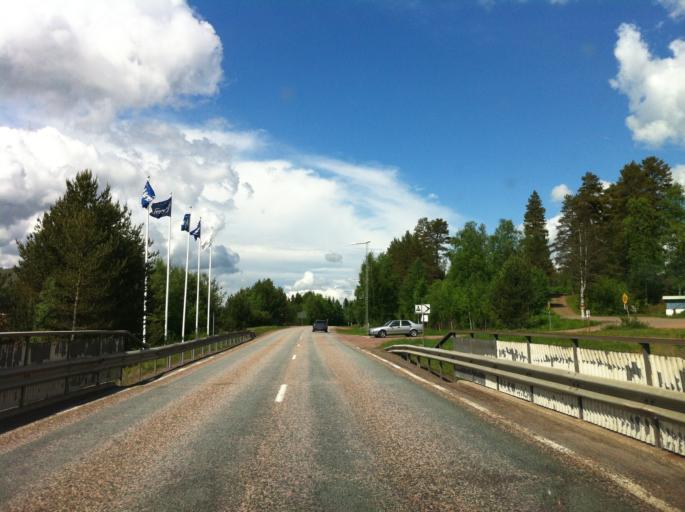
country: SE
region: Dalarna
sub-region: Malung-Saelens kommun
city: Malung
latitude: 61.0358
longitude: 13.3378
